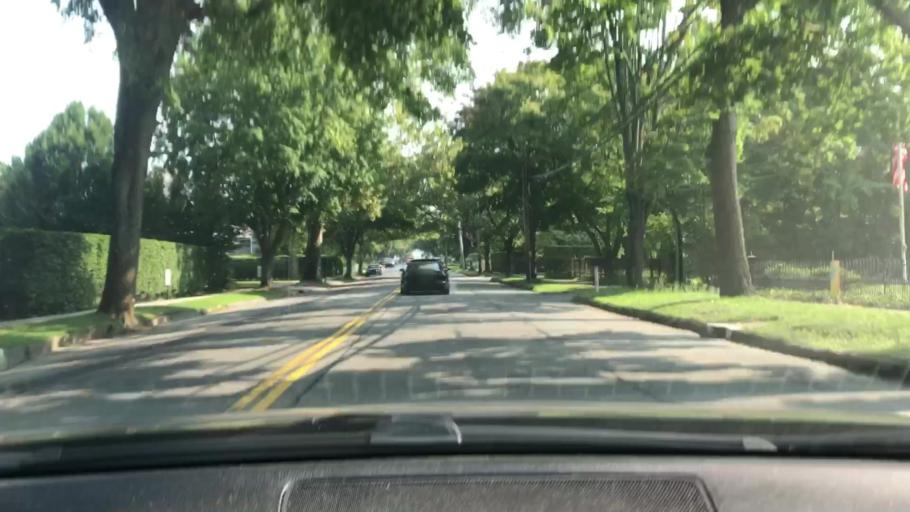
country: US
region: New York
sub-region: Suffolk County
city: Sag Harbor
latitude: 40.9957
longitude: -72.2982
